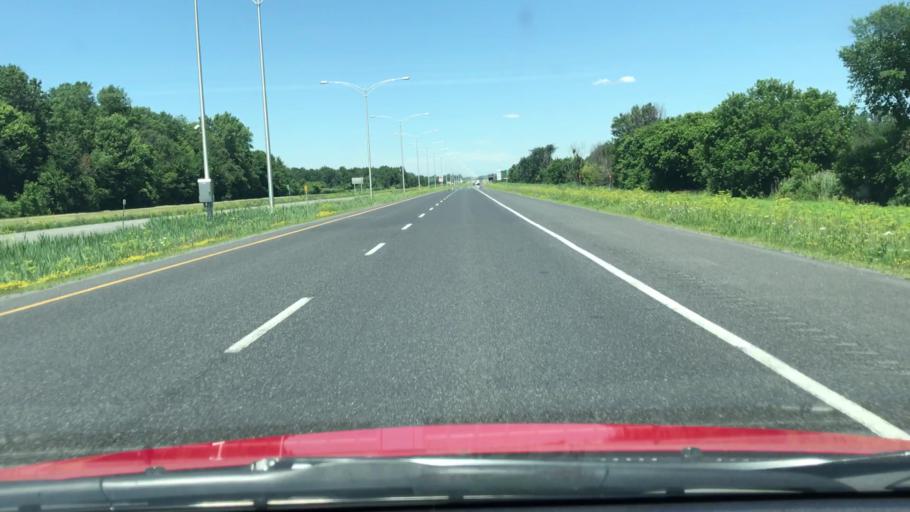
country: US
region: New York
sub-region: Clinton County
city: Champlain
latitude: 45.0238
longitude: -73.4529
